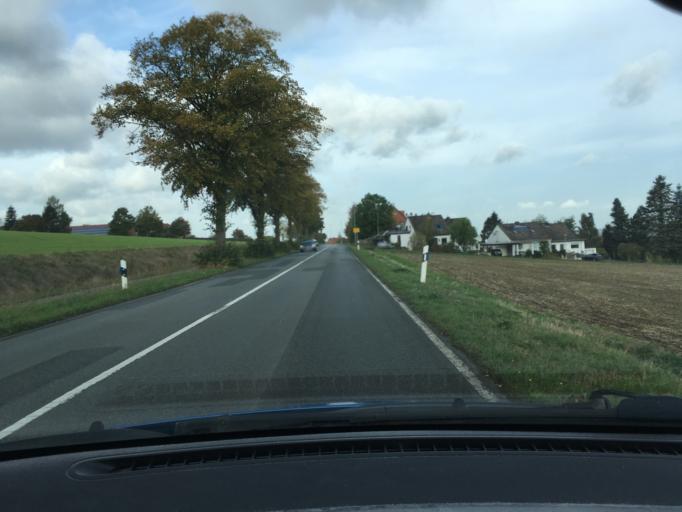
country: DE
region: Lower Saxony
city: Barsinghausen
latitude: 52.3246
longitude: 9.4201
